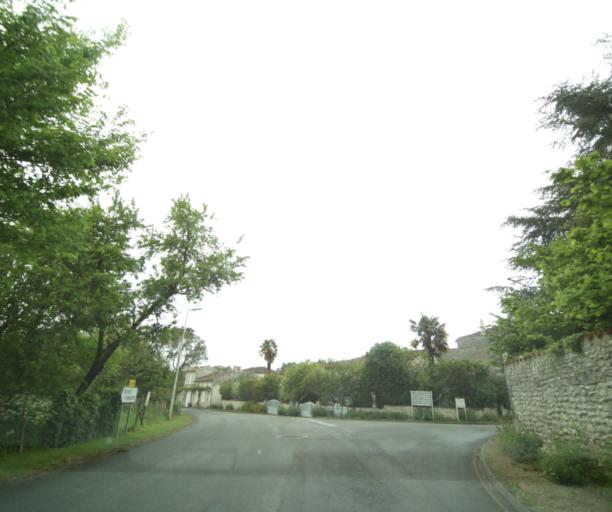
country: FR
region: Poitou-Charentes
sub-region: Departement de la Charente-Maritime
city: Cherac
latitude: 45.6850
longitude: -0.4902
